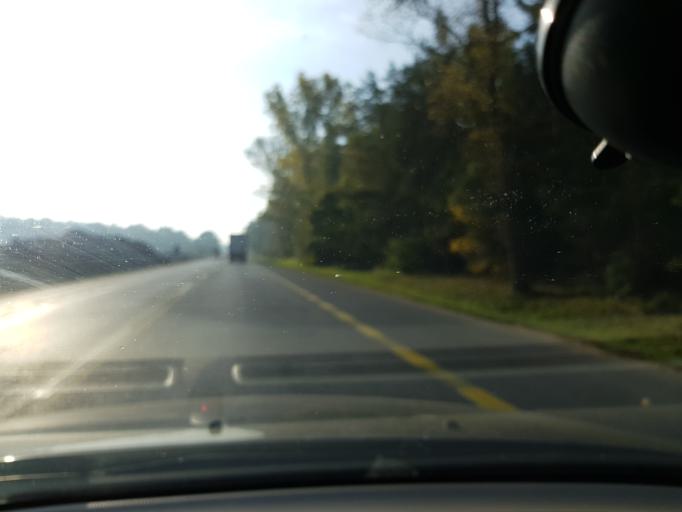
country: PL
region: Masovian Voivodeship
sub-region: Powiat otwocki
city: Otwock
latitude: 52.1497
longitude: 21.3183
